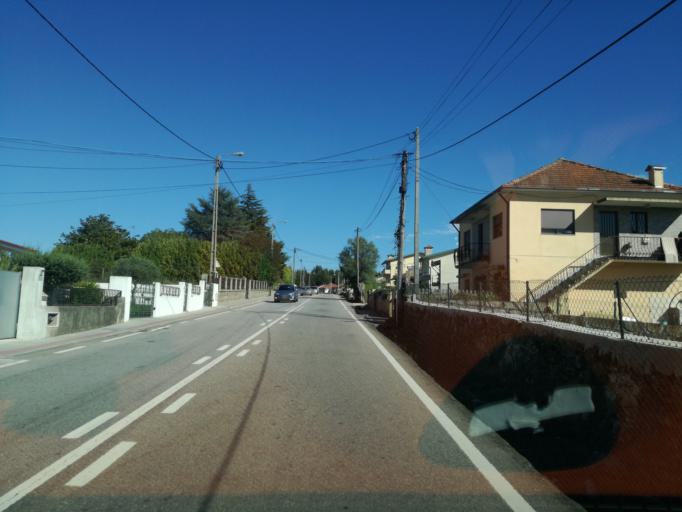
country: PT
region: Porto
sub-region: Trofa
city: Sao Romao do Coronado
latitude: 41.2759
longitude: -8.5461
